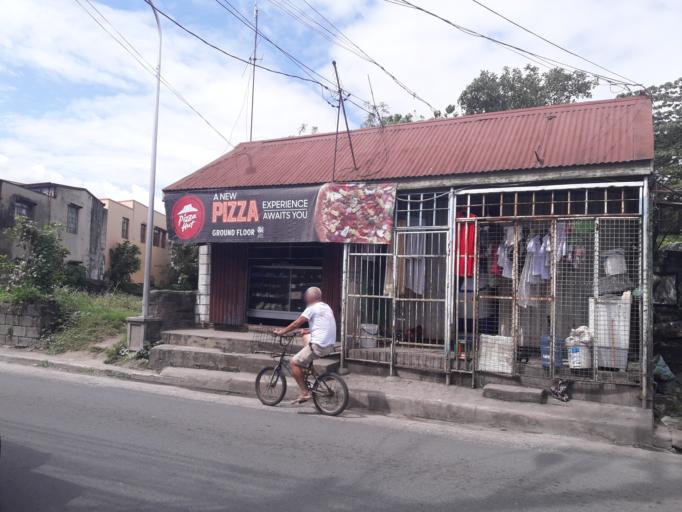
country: PH
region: Calabarzon
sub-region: Province of Laguna
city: Santa Rosa
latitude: 14.3058
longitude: 121.1100
